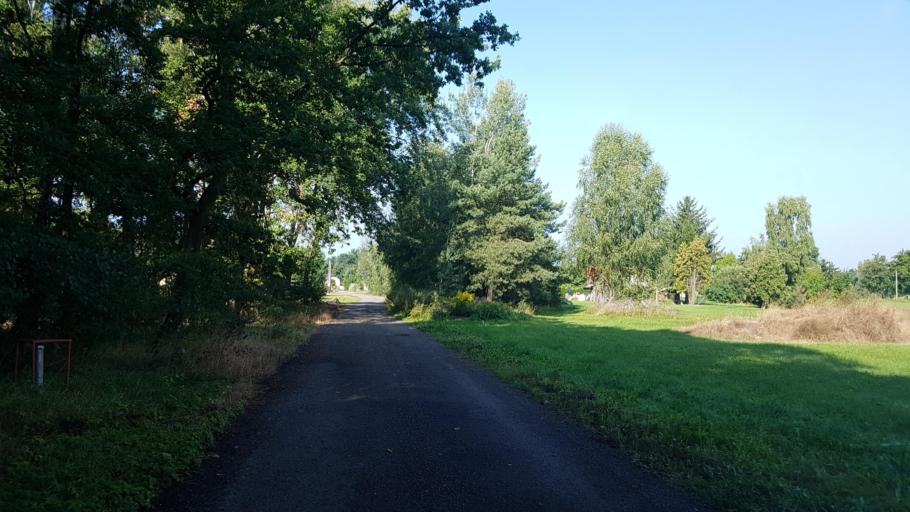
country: DE
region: Brandenburg
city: Luckau
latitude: 51.7990
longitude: 13.6506
